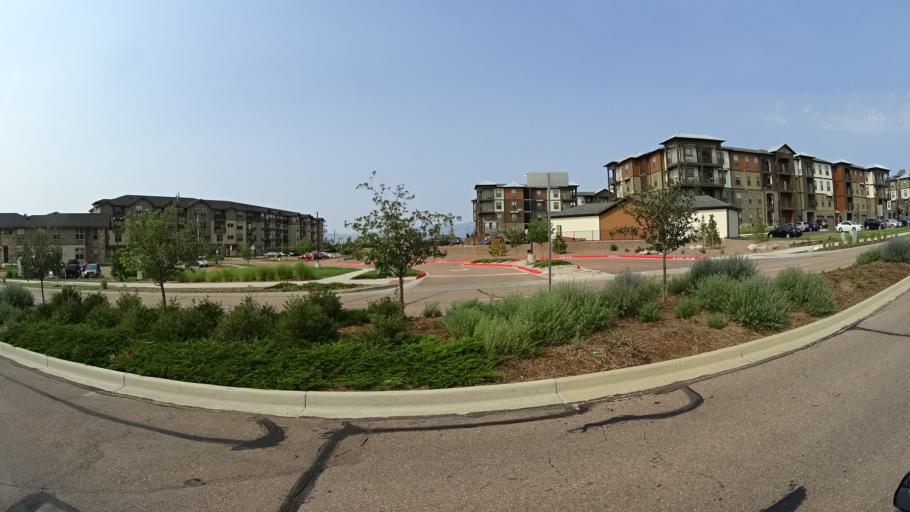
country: US
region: Colorado
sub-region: El Paso County
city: Black Forest
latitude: 38.9617
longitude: -104.7308
